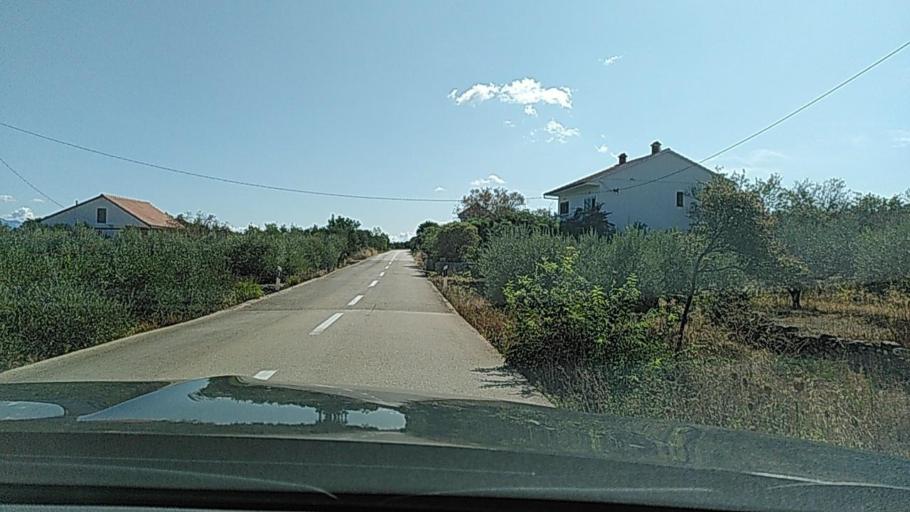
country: HR
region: Splitsko-Dalmatinska
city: Jelsa
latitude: 43.1490
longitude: 16.7946
